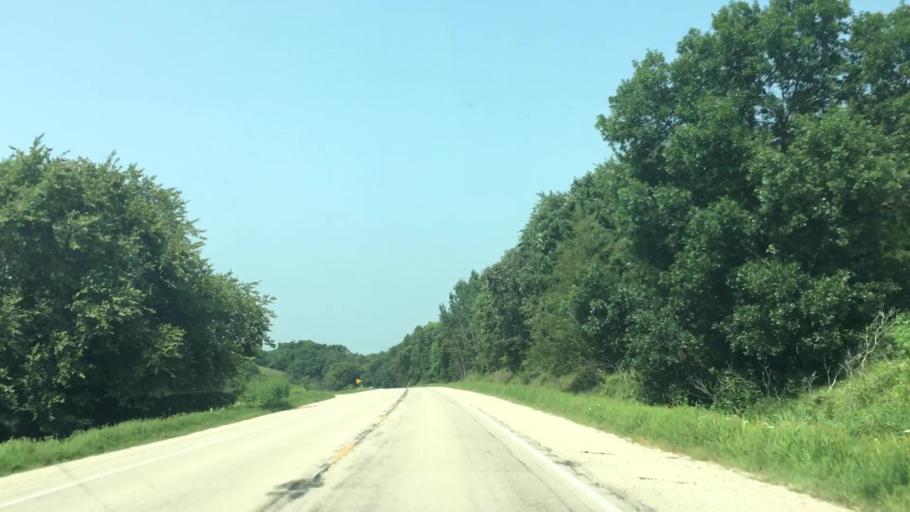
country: US
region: Iowa
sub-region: Fayette County
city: West Union
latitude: 43.0726
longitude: -91.8389
